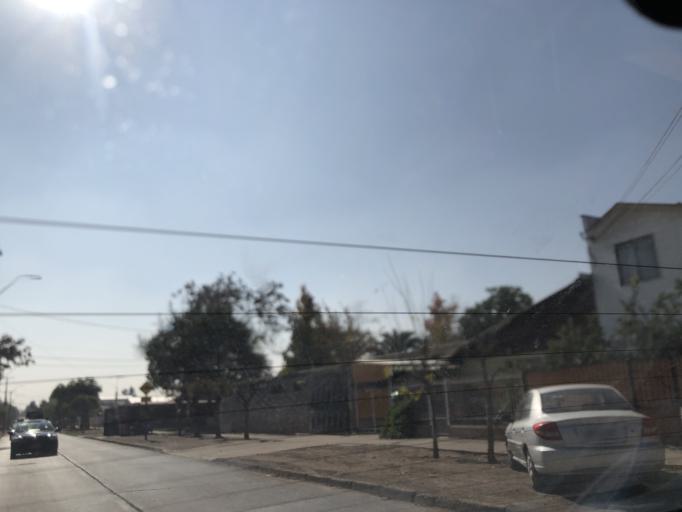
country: CL
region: Santiago Metropolitan
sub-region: Provincia de Cordillera
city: Puente Alto
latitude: -33.6263
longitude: -70.5876
